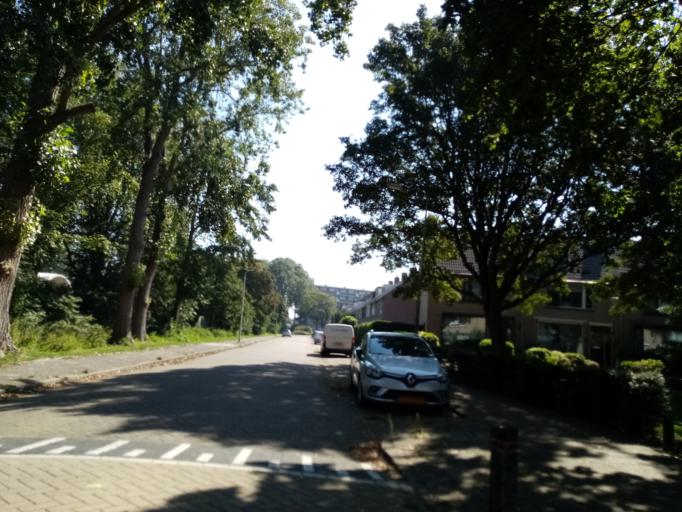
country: NL
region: South Holland
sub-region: Gemeente Lisse
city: Lisse
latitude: 52.2451
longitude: 4.5622
